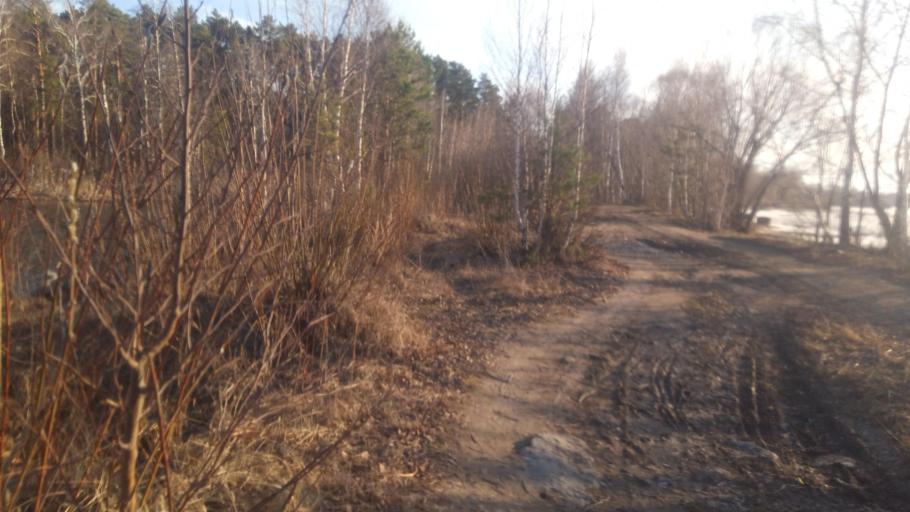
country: RU
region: Chelyabinsk
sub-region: Gorod Chelyabinsk
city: Chelyabinsk
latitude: 55.1401
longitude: 61.3307
